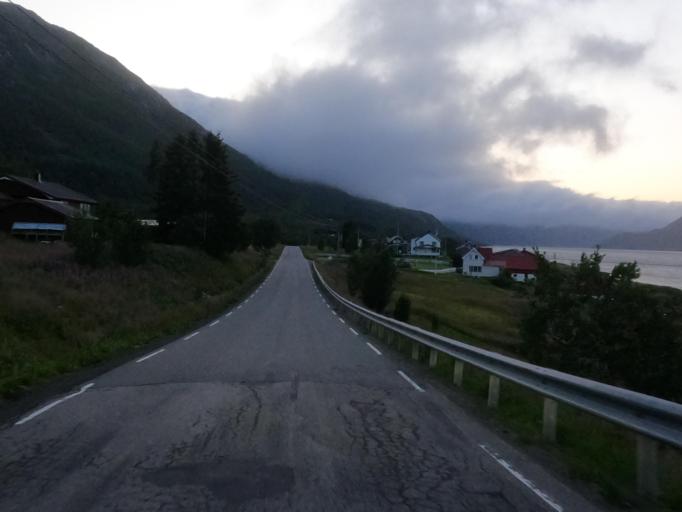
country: NO
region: Nordland
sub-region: Lodingen
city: Lodingen
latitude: 68.5674
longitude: 15.7996
